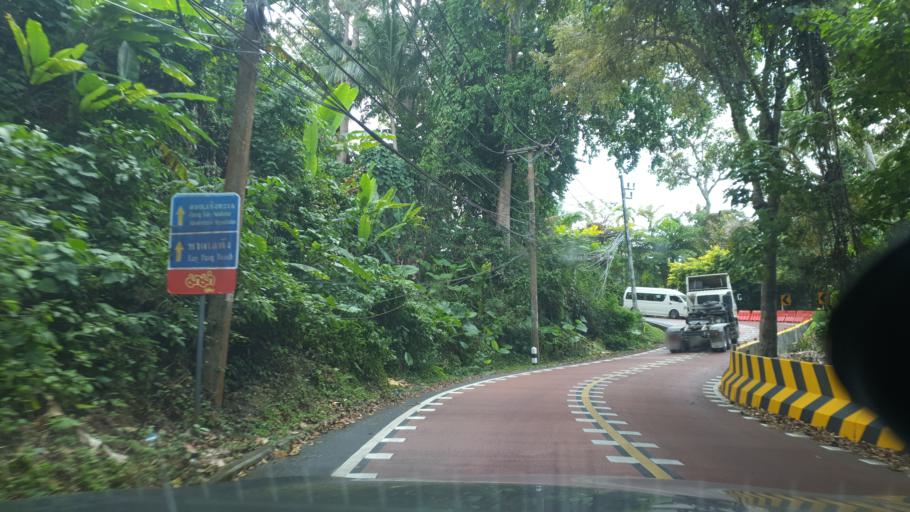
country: TH
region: Phuket
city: Thalang
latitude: 8.0403
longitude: 98.2754
